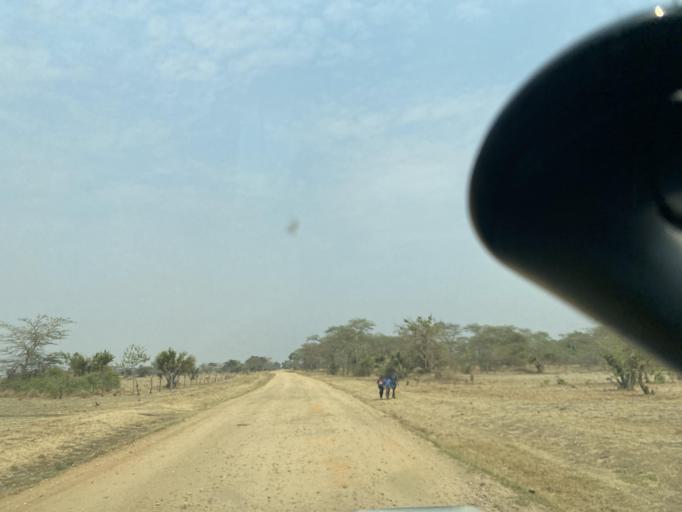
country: ZM
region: Lusaka
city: Kafue
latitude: -15.6479
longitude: 28.0405
